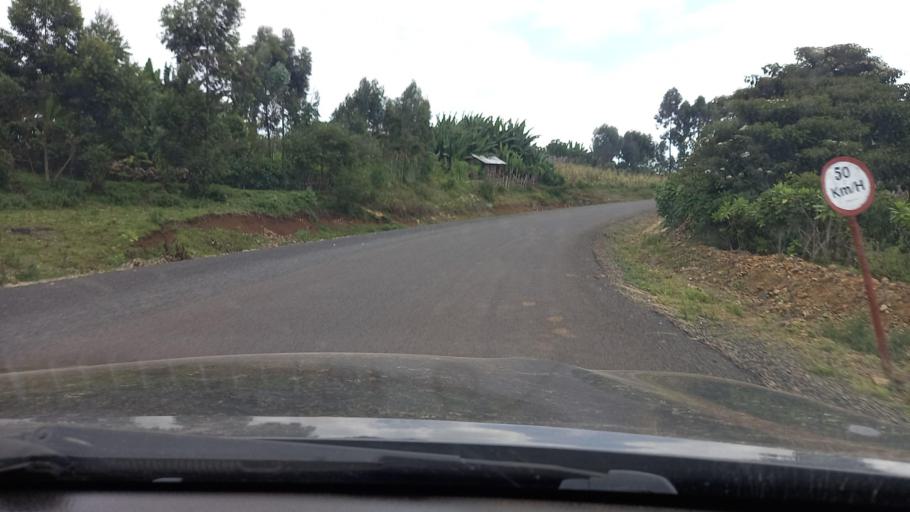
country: ET
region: Southern Nations, Nationalities, and People's Region
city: Mizan Teferi
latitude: 6.2110
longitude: 35.6141
